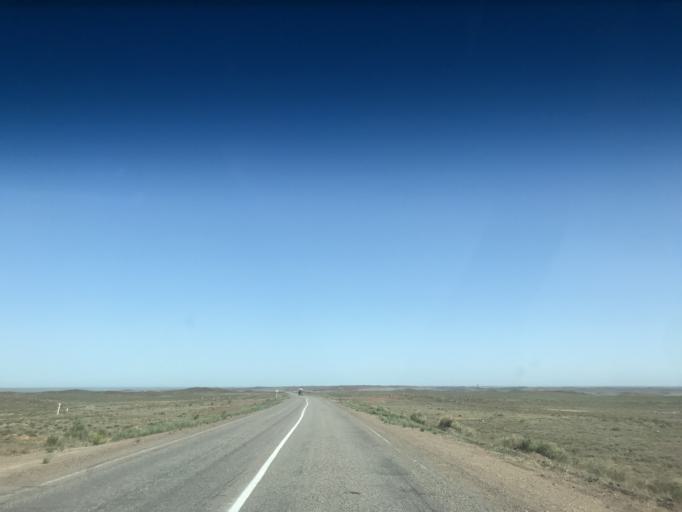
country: KZ
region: Zhambyl
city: Mynaral
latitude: 45.4702
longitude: 73.5584
